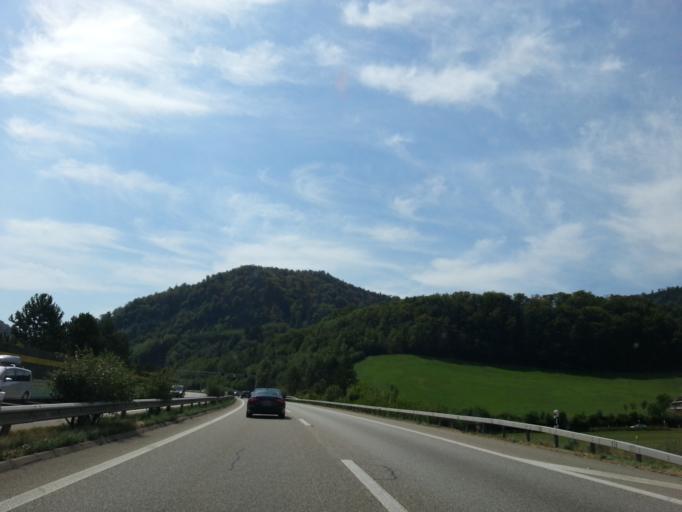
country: CH
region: Basel-Landschaft
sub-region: Bezirk Waldenburg
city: Diegten
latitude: 47.4045
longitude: 7.8068
